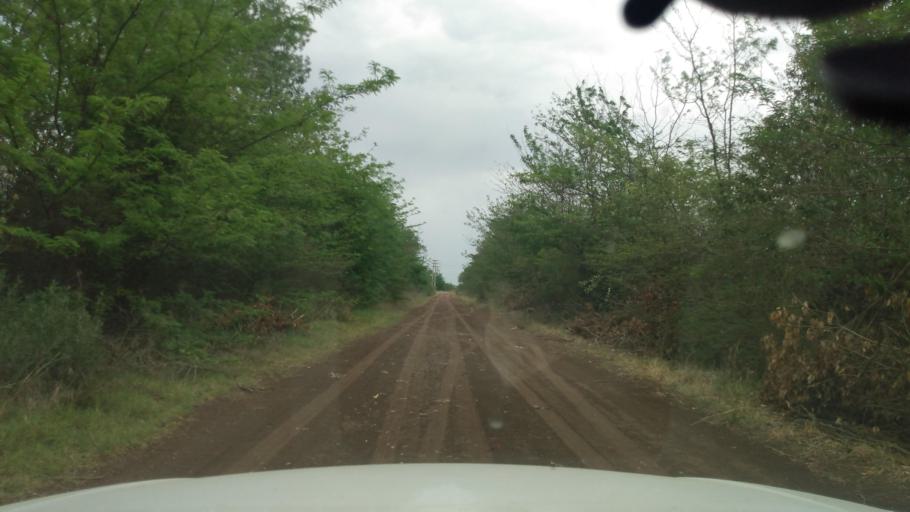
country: AR
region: Buenos Aires
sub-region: Partido de Lujan
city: Lujan
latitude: -34.5498
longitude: -59.1668
